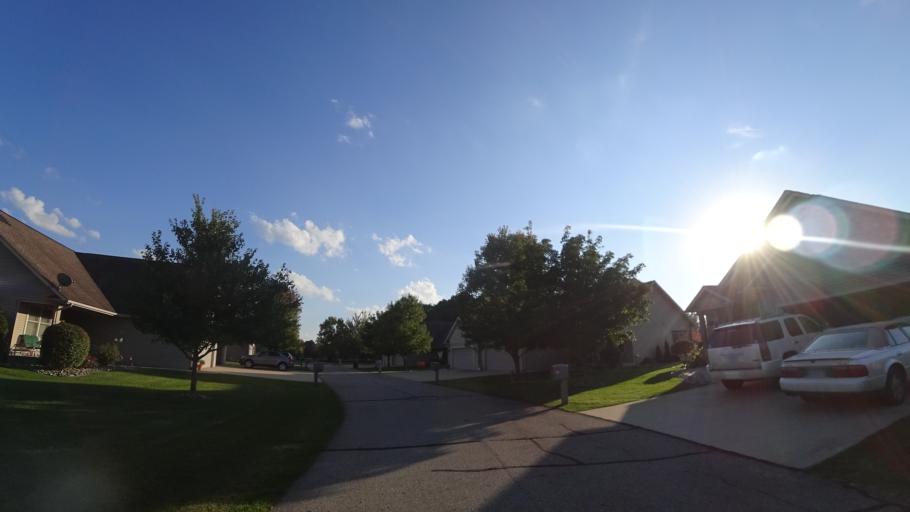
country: US
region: Michigan
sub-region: Saint Joseph County
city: Three Rivers
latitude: 41.9656
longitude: -85.6319
